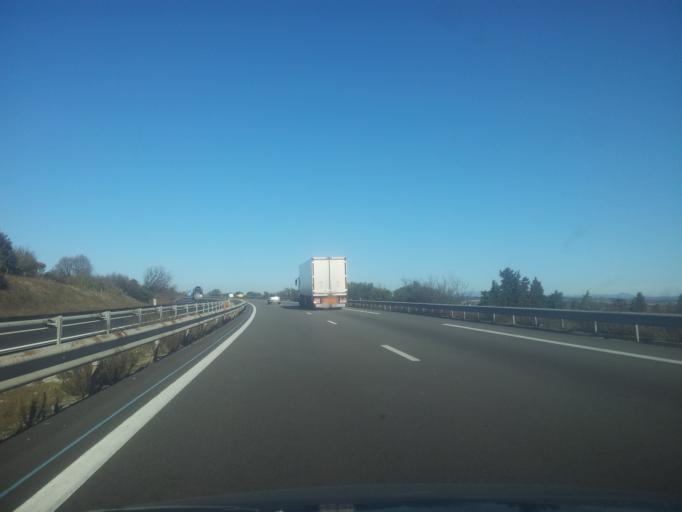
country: FR
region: Languedoc-Roussillon
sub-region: Departement du Gard
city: Roquemaure
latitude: 44.0386
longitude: 4.7647
